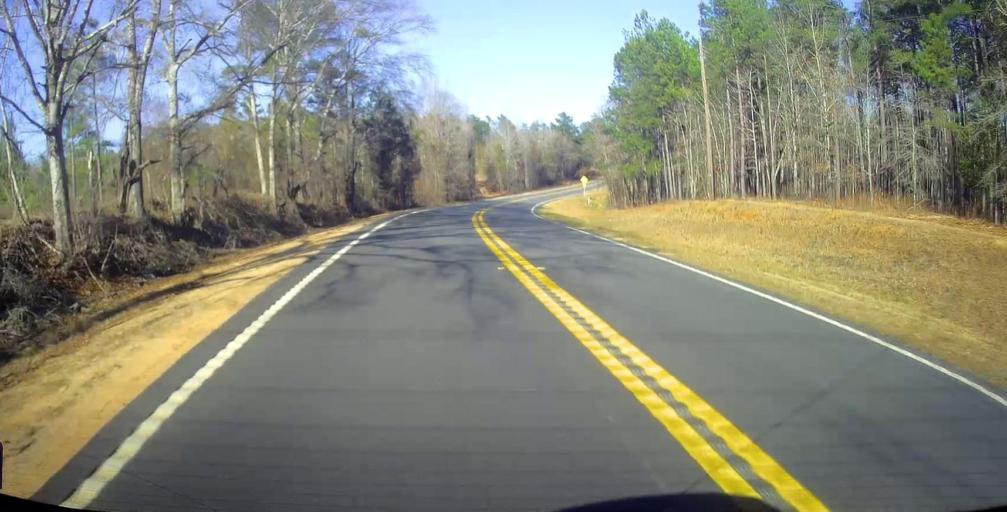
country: US
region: Georgia
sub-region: Taylor County
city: Butler
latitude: 32.6533
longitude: -84.3679
